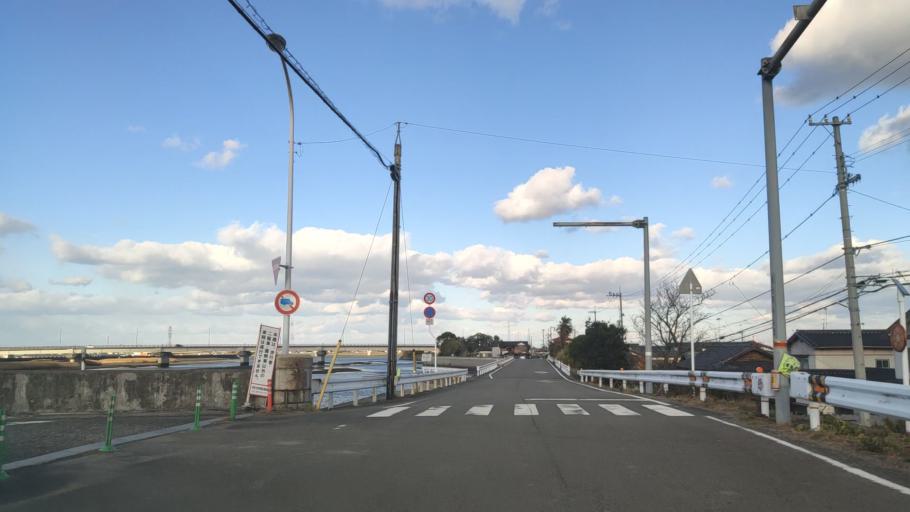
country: JP
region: Ehime
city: Saijo
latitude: 33.9079
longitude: 133.1298
